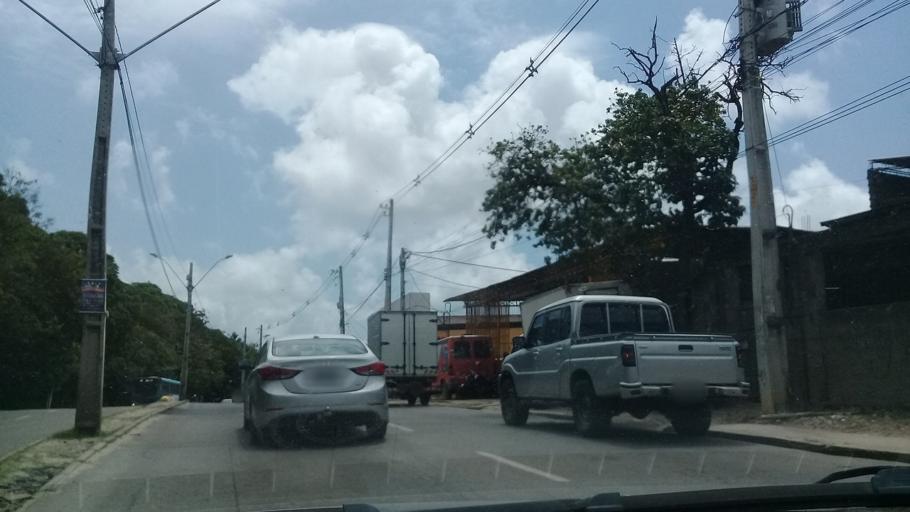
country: BR
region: Pernambuco
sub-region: Recife
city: Recife
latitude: -8.1074
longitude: -34.9299
